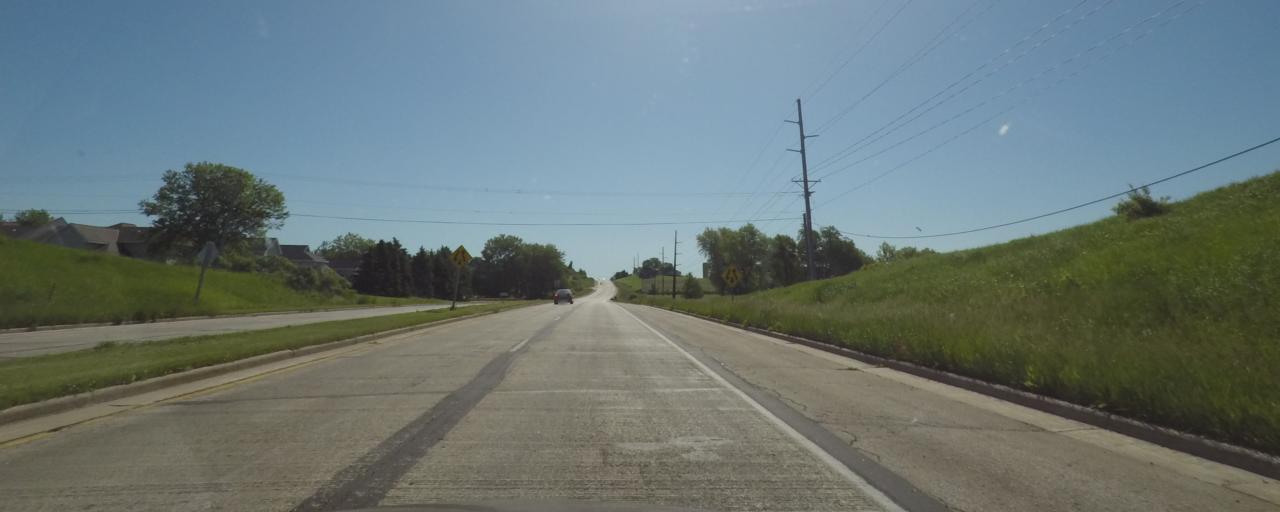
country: US
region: Wisconsin
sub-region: Fond du Lac County
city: Fond du Lac
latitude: 43.7836
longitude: -88.3772
